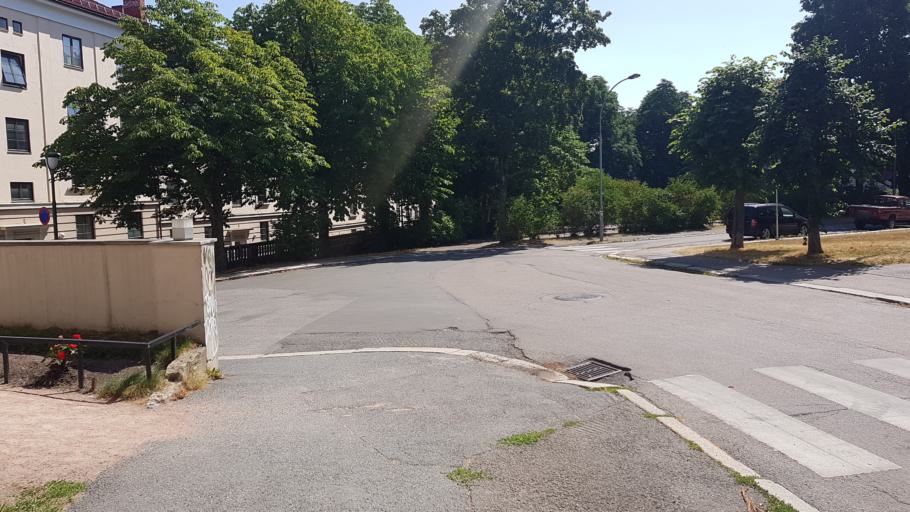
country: NO
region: Oslo
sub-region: Oslo
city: Oslo
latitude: 59.9302
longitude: 10.7472
